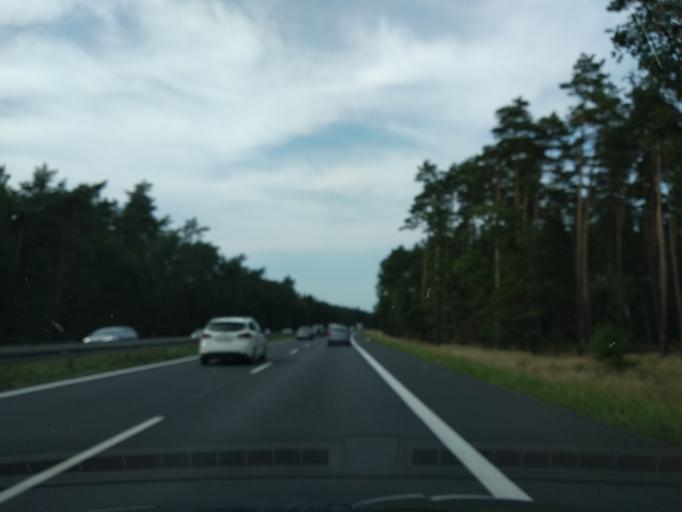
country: PL
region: West Pomeranian Voivodeship
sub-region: Powiat goleniowski
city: Goleniow
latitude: 53.5564
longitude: 14.7962
